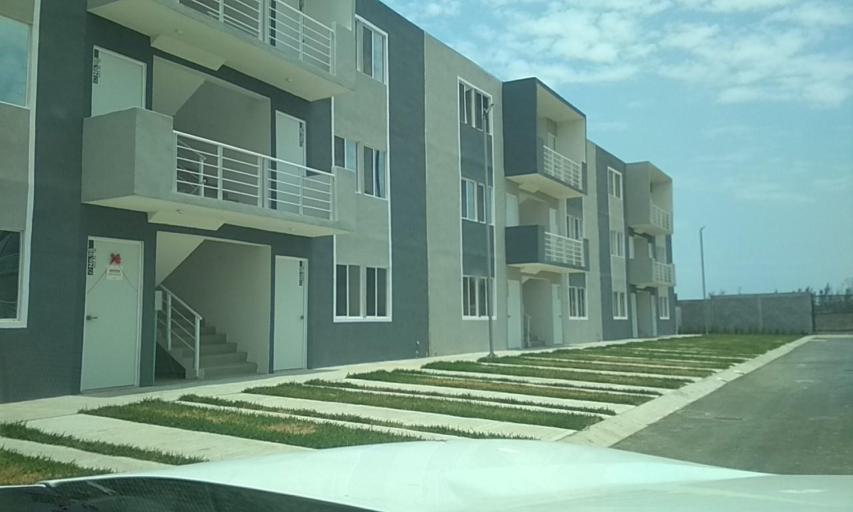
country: MX
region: Veracruz
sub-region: Veracruz
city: Las Amapolas
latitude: 19.1475
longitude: -96.2158
